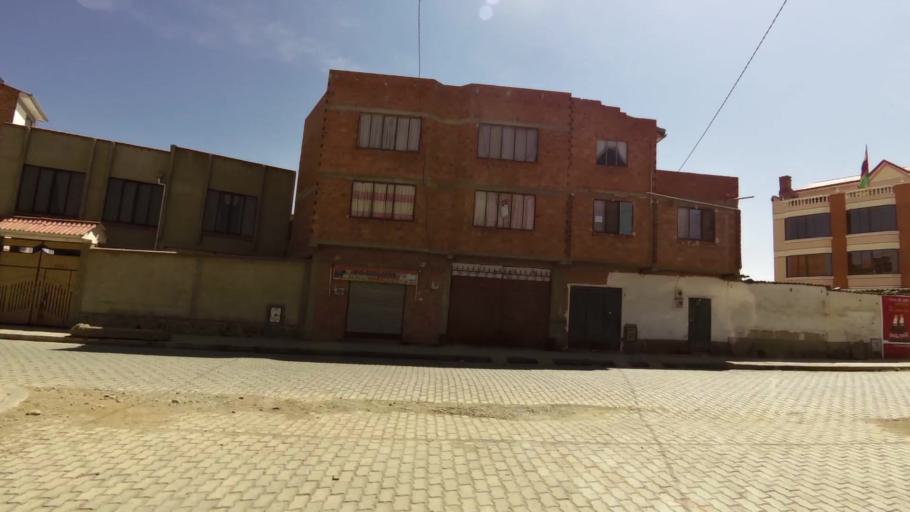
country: BO
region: La Paz
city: La Paz
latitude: -16.5376
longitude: -68.1553
